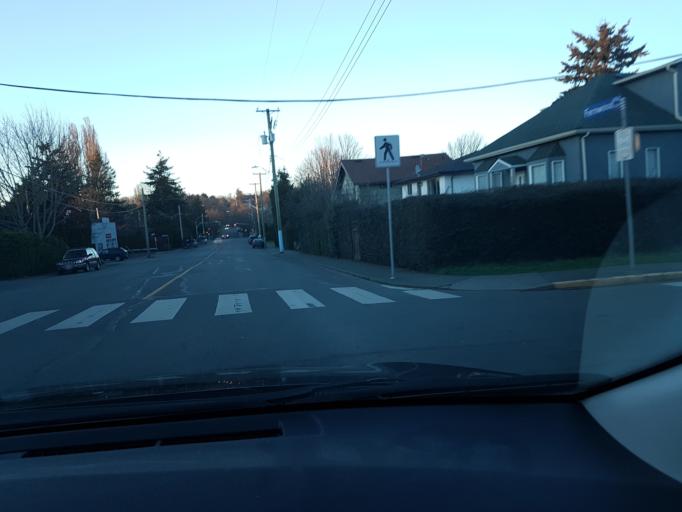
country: CA
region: British Columbia
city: Victoria
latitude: 48.4328
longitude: -123.3451
